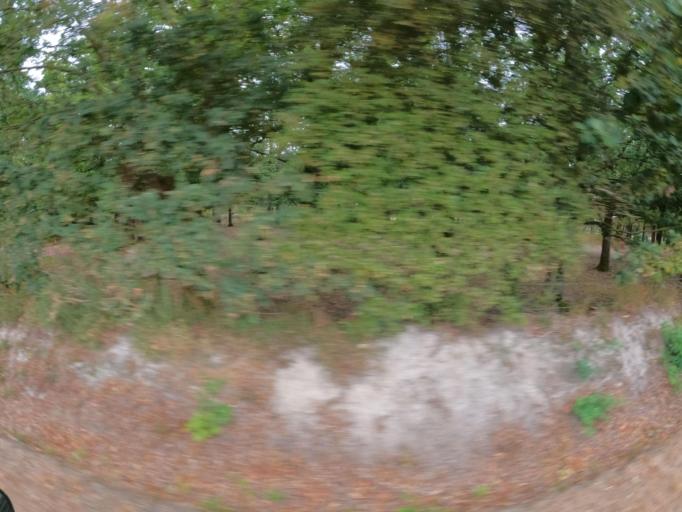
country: FR
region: Pays de la Loire
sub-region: Departement de la Vendee
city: Montaigu
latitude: 46.9753
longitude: -1.2968
